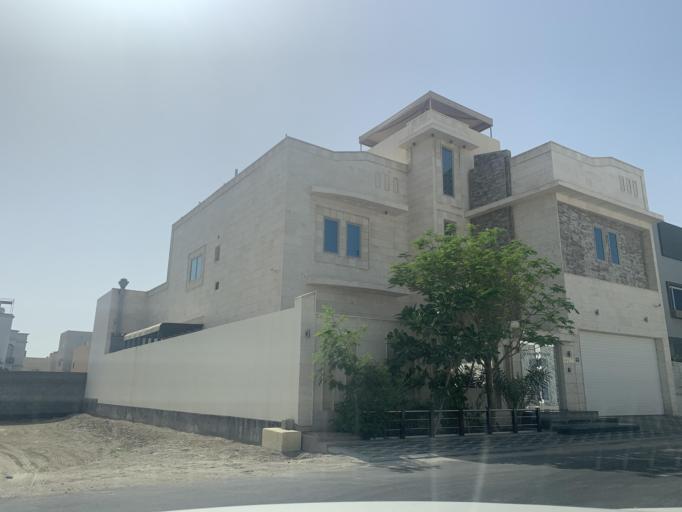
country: BH
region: Northern
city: Sitrah
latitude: 26.1667
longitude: 50.6285
